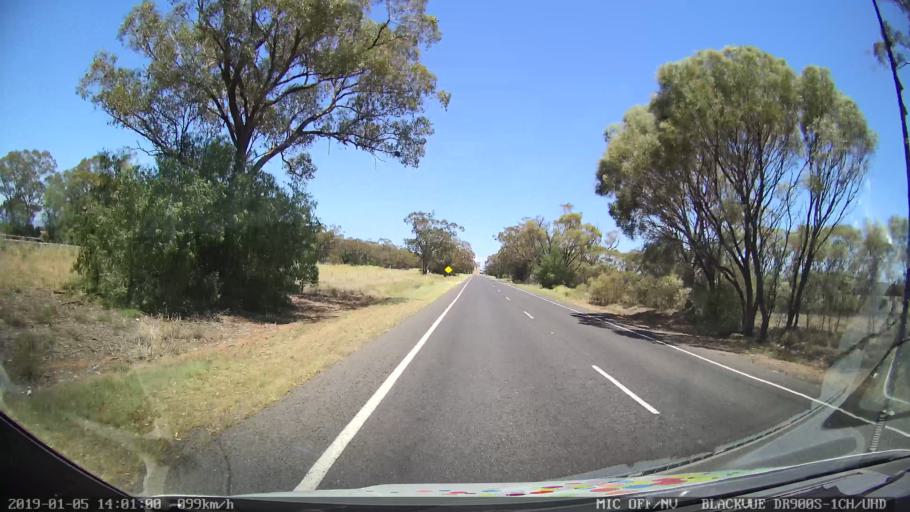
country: AU
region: New South Wales
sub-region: Gunnedah
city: Gunnedah
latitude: -31.1653
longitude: 150.3194
